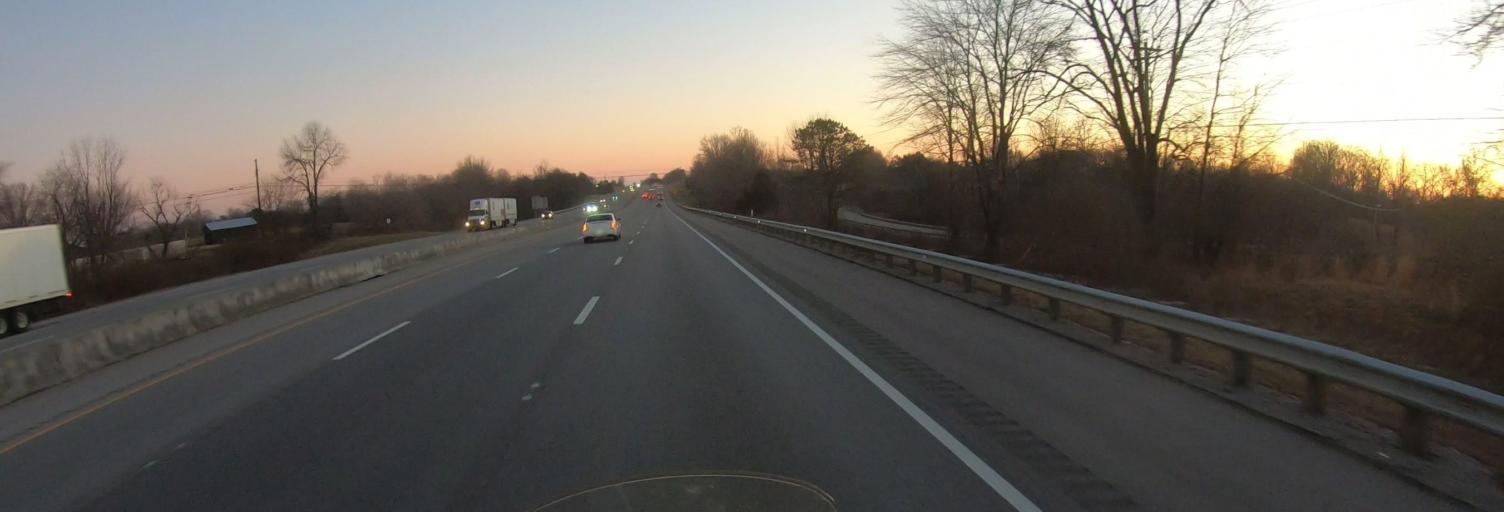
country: US
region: Kentucky
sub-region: Laurel County
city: London
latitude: 37.0781
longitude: -84.0995
